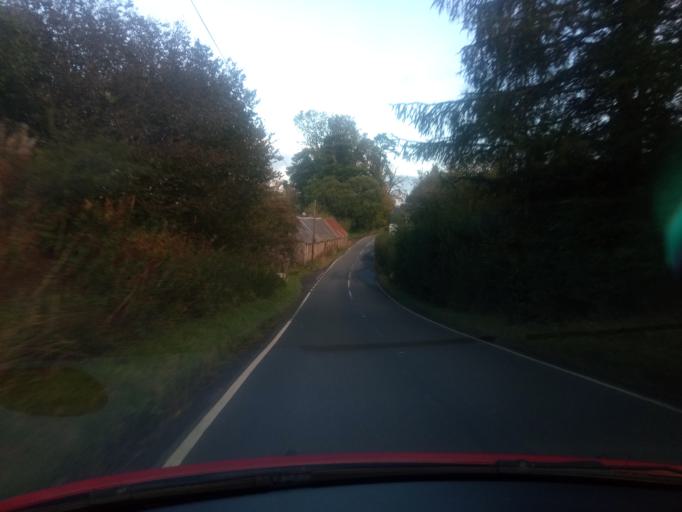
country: GB
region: Scotland
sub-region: The Scottish Borders
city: Hawick
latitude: 55.3643
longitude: -2.6506
